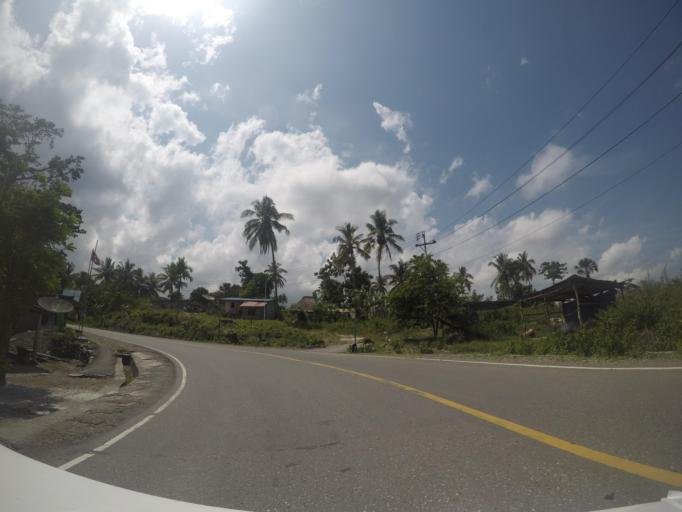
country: TL
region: Baucau
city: Baucau
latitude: -8.4879
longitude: 126.3461
